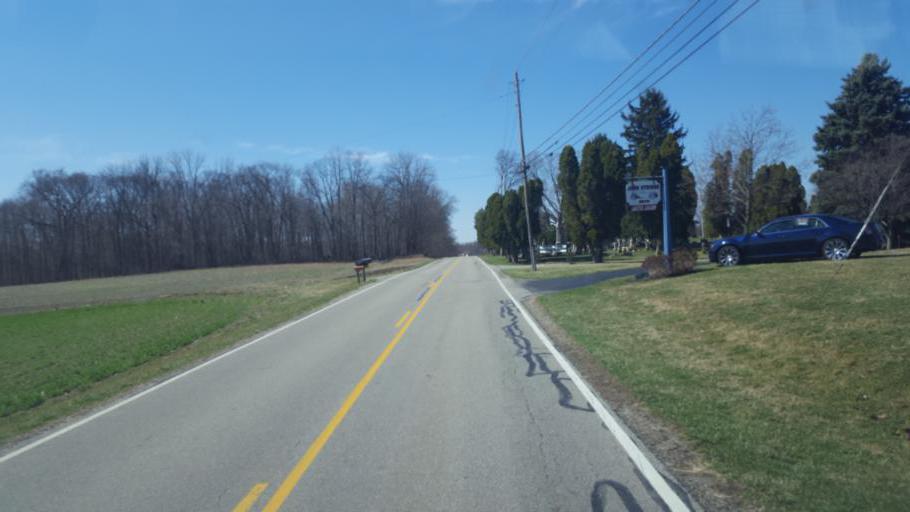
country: US
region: Ohio
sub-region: Marion County
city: Prospect
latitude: 40.5279
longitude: -83.1979
